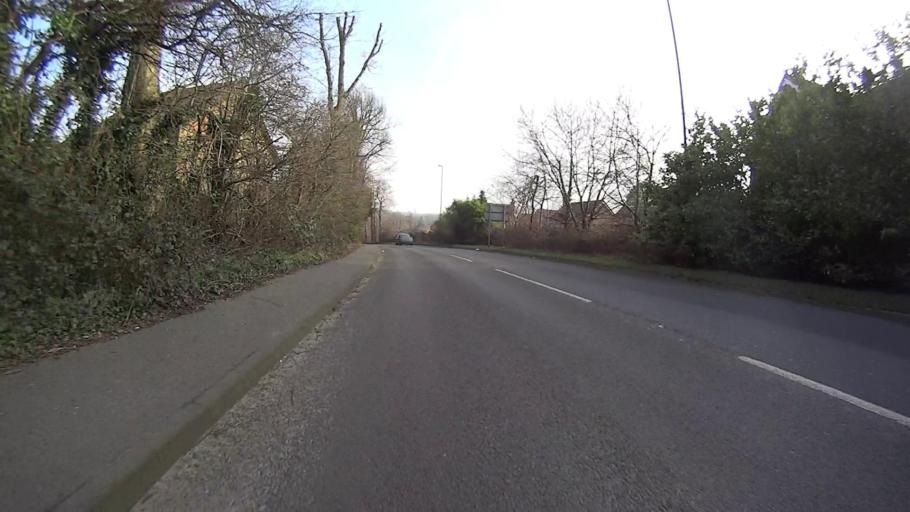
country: GB
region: England
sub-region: West Sussex
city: Maidenbower
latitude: 51.1111
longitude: -0.1468
